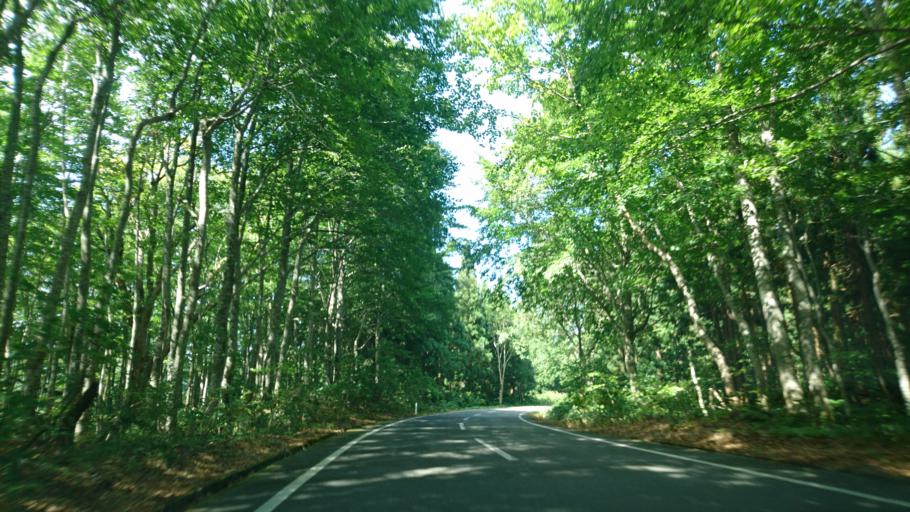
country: JP
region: Akita
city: Yuzawa
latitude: 38.9714
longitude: 140.7119
